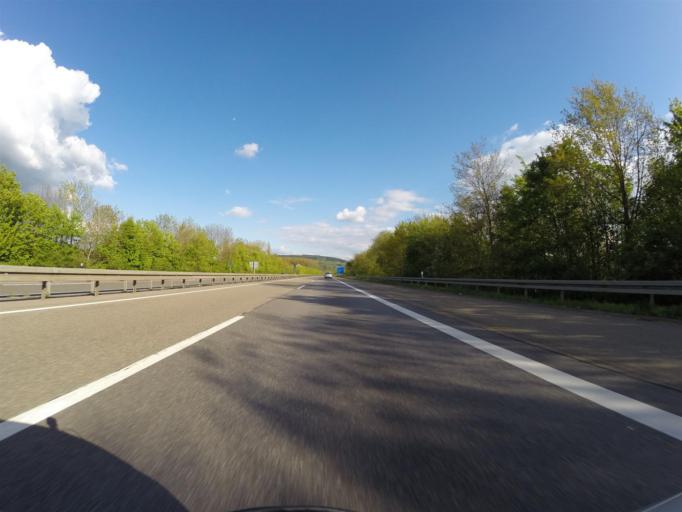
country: DE
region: Saarland
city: Merzig
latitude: 49.4510
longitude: 6.6162
